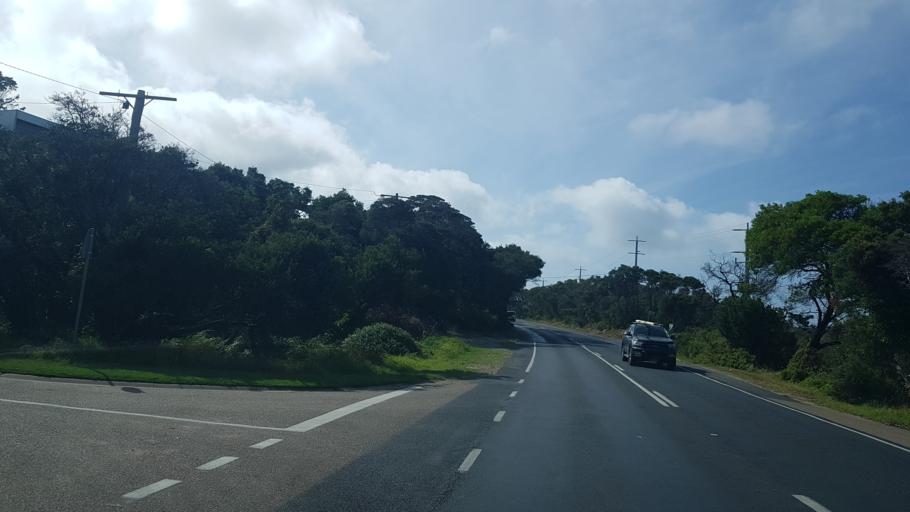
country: AU
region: Victoria
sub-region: Mornington Peninsula
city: Blairgowrie
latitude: -38.3656
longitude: 144.7666
